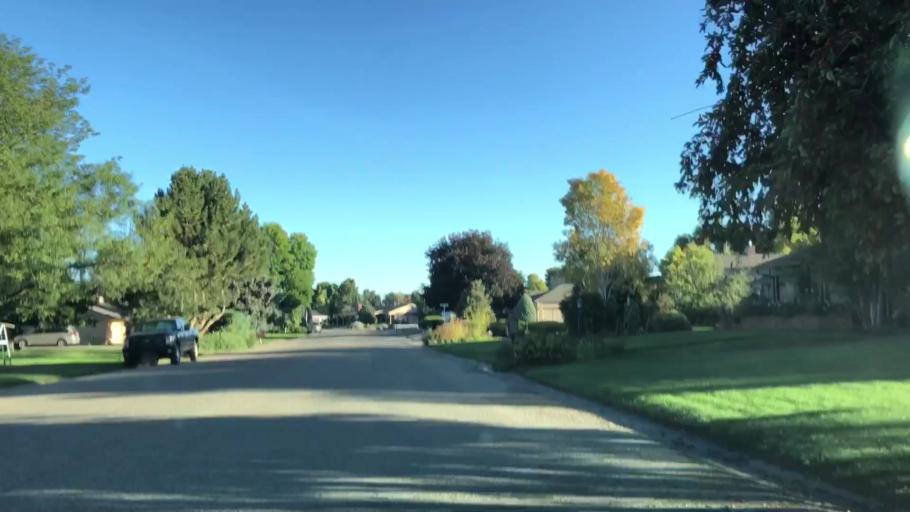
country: US
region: Colorado
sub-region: Larimer County
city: Loveland
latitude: 40.4280
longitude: -105.0220
